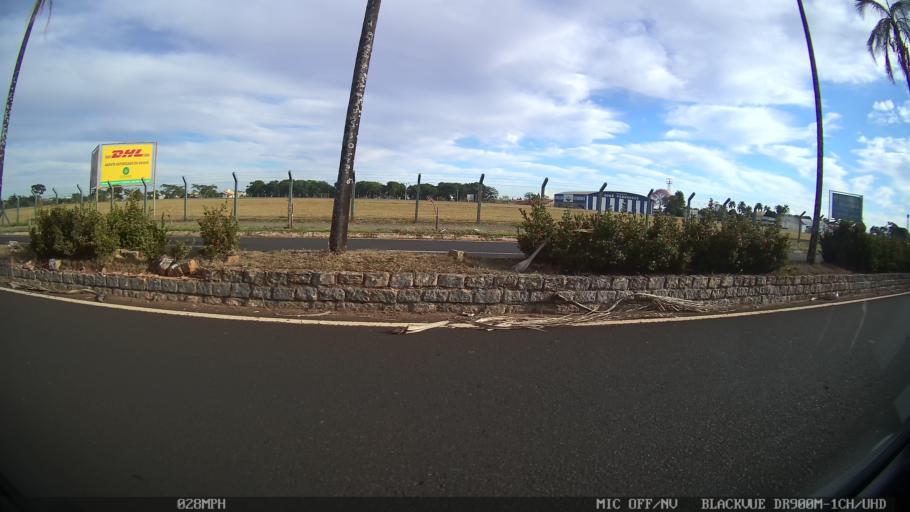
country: BR
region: Sao Paulo
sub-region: Catanduva
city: Catanduva
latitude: -21.1476
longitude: -48.9861
